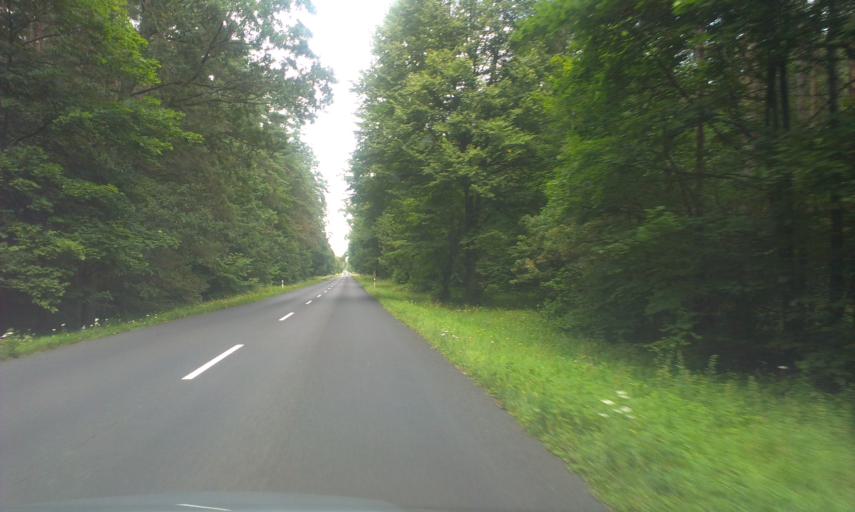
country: PL
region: West Pomeranian Voivodeship
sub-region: Powiat bialogardzki
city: Bialogard
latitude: 53.9193
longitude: 16.0655
